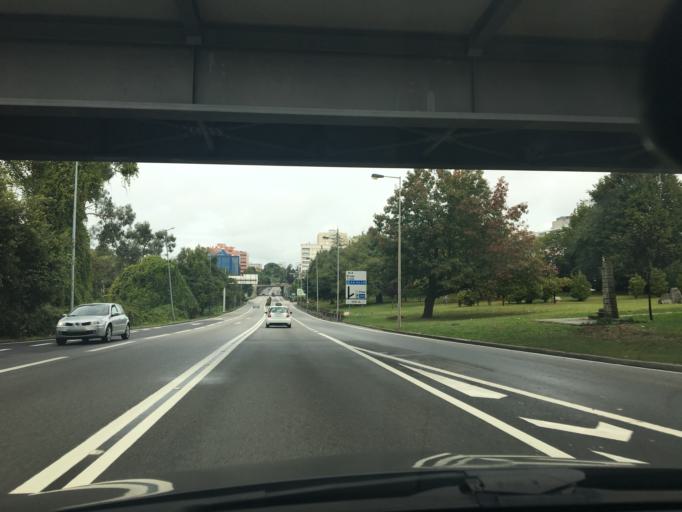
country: PT
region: Porto
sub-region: Maia
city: Maia
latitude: 41.2290
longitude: -8.6265
